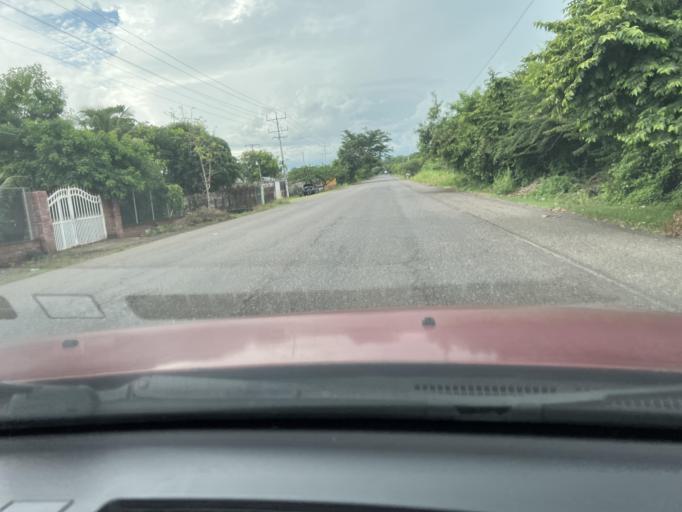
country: SV
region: La Union
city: San Alejo
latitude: 13.4176
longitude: -87.8877
